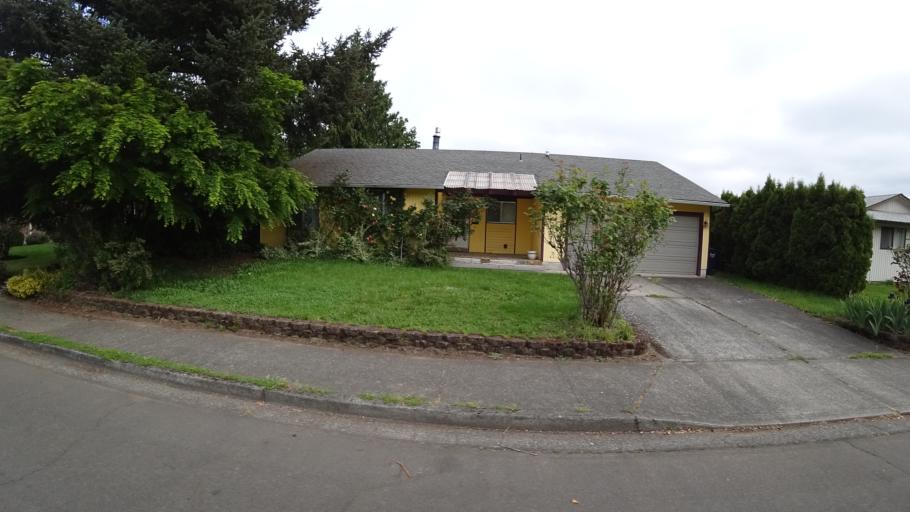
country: US
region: Oregon
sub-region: Washington County
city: Aloha
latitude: 45.5135
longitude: -122.8743
